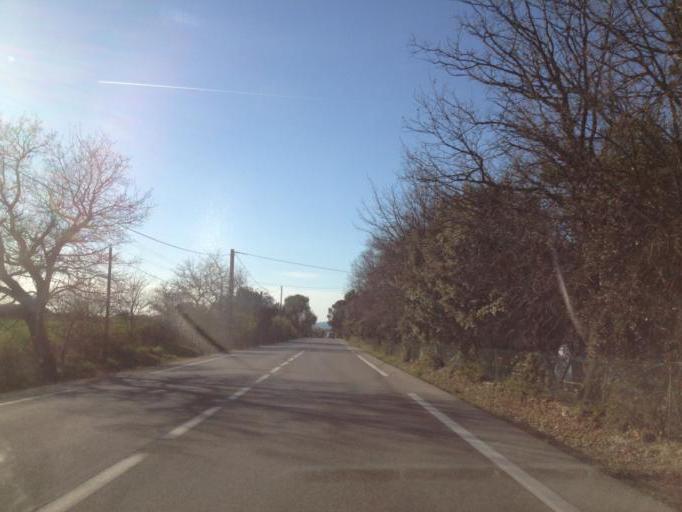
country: FR
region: Provence-Alpes-Cote d'Azur
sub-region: Departement des Bouches-du-Rhone
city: Eguilles
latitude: 43.6057
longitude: 5.3369
